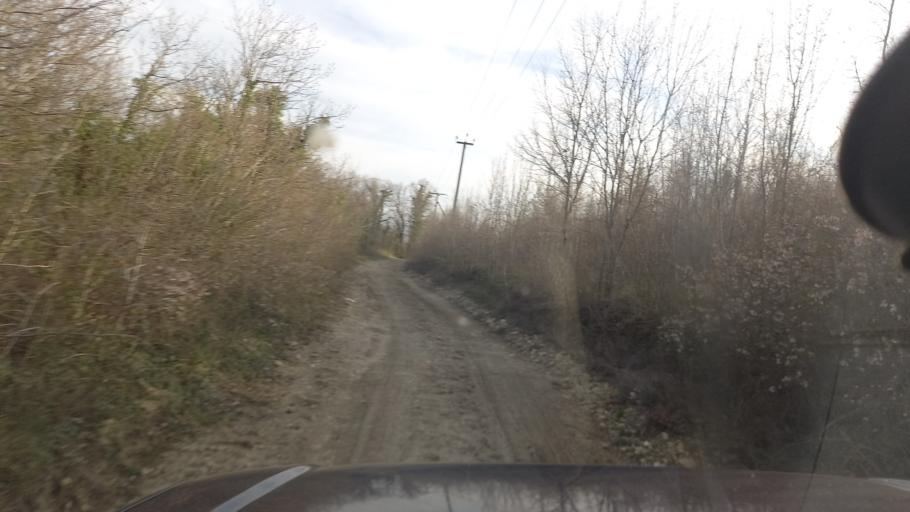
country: RU
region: Krasnodarskiy
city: Arkhipo-Osipovka
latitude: 44.3614
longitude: 38.5641
